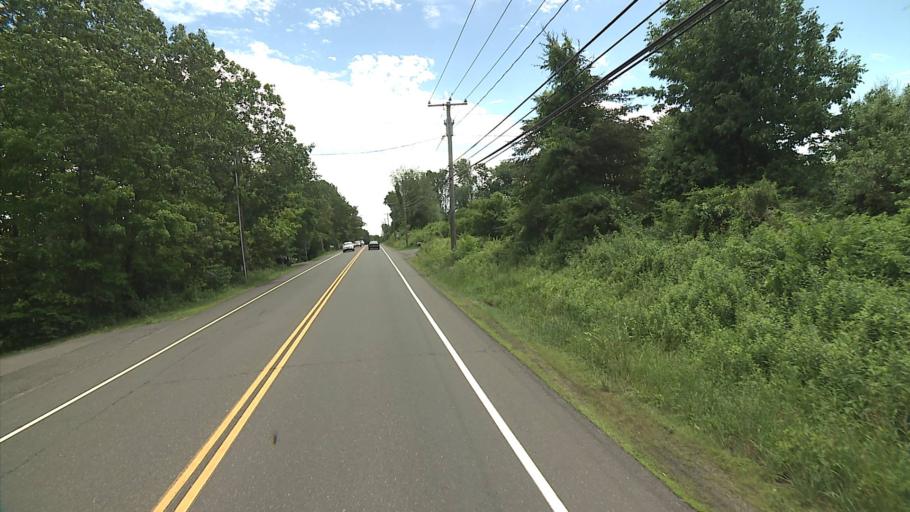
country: US
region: Connecticut
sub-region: Litchfield County
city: Watertown
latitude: 41.6445
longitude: -73.1479
